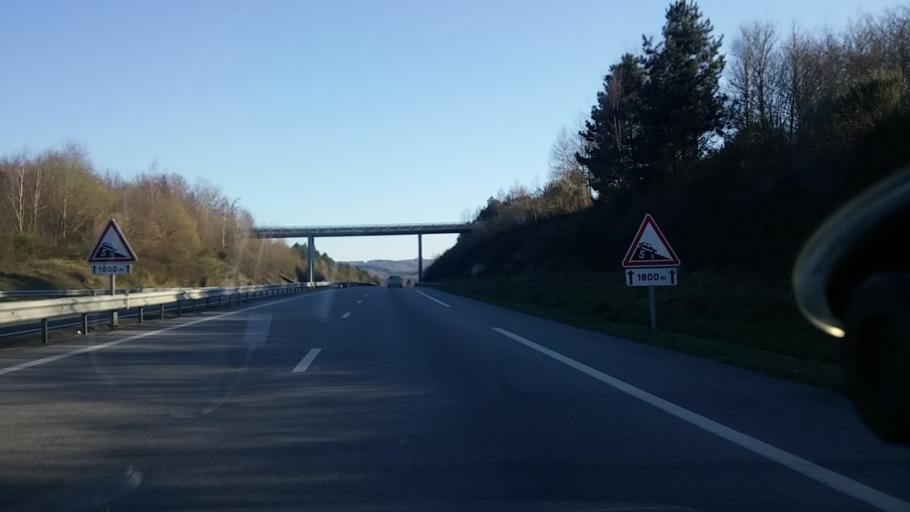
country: FR
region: Limousin
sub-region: Departement de la Haute-Vienne
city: Bessines-sur-Gartempe
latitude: 46.1342
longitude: 1.3808
